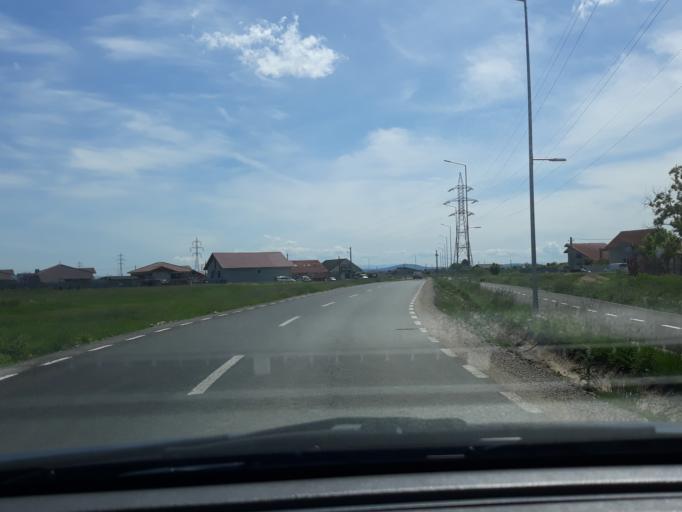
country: RO
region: Bihor
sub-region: Comuna Santandrei
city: Santandrei
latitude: 47.0689
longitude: 21.8605
